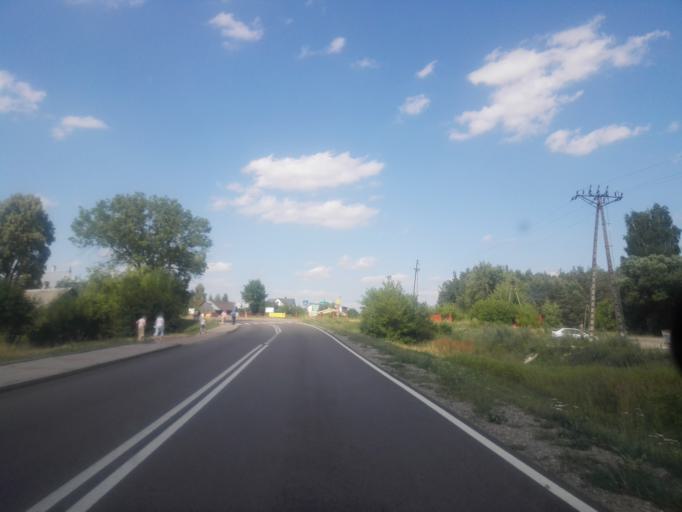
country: PL
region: Podlasie
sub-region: Powiat sejnenski
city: Sejny
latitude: 54.0364
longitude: 23.3566
